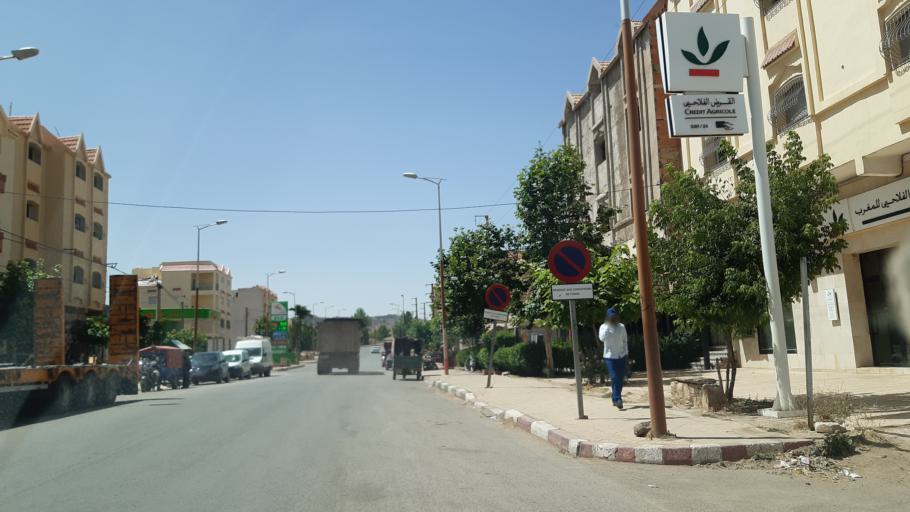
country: MA
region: Meknes-Tafilalet
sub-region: Ifrane
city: Azrou
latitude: 33.2340
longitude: -5.0583
